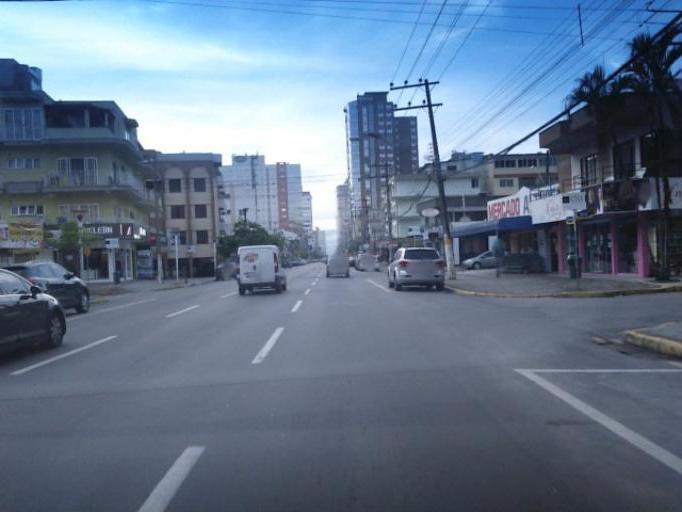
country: BR
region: Santa Catarina
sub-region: Itapema
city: Itapema
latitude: -27.1326
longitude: -48.5989
